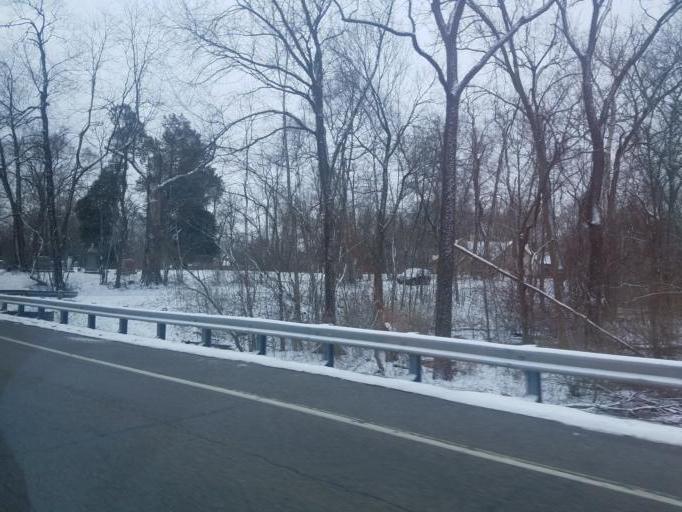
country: US
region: Ohio
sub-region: Franklin County
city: New Albany
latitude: 40.0437
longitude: -82.8079
